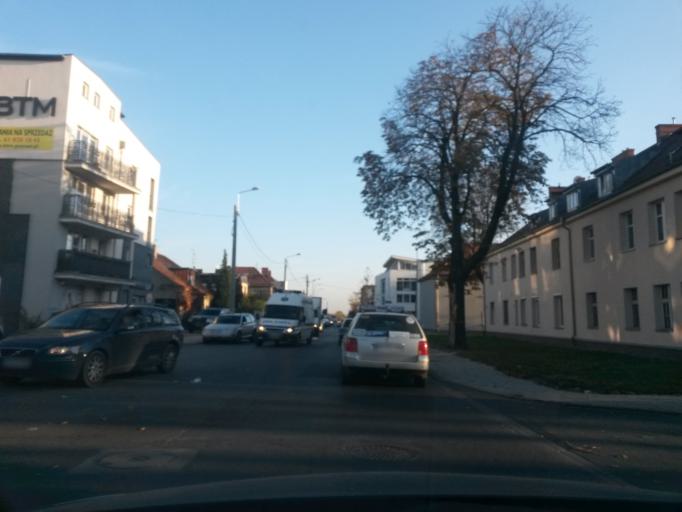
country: PL
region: Greater Poland Voivodeship
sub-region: Powiat poznanski
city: Lubon
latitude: 52.3826
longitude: 16.8852
